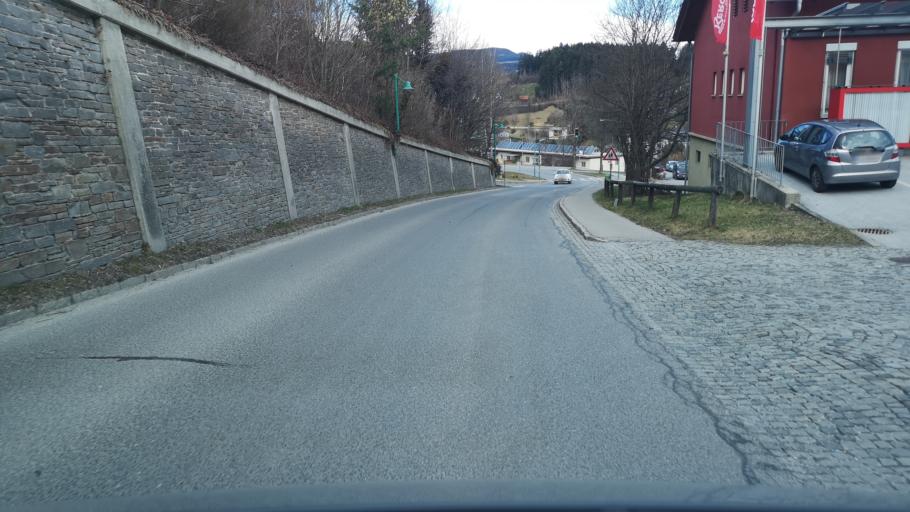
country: AT
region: Styria
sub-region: Politischer Bezirk Weiz
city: Birkfeld
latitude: 47.3548
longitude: 15.6927
